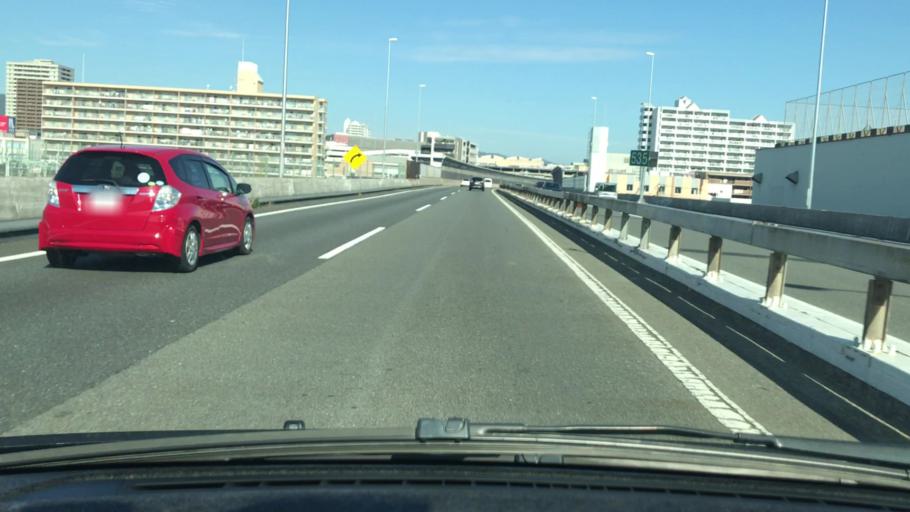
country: JP
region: Hyogo
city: Nishinomiya-hama
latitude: 34.7378
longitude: 135.3595
